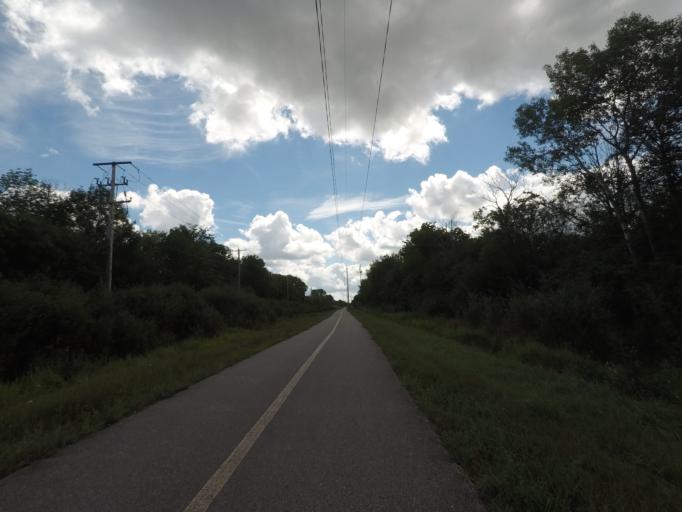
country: US
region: Wisconsin
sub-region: Waukesha County
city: Pewaukee
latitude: 43.0524
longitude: -88.2815
